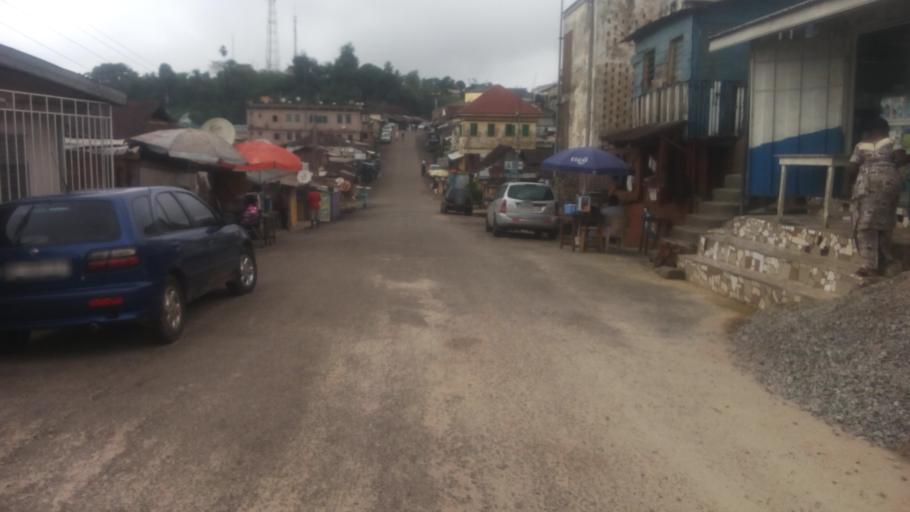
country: GH
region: Western
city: Tarkwa
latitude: 5.3039
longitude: -1.9893
